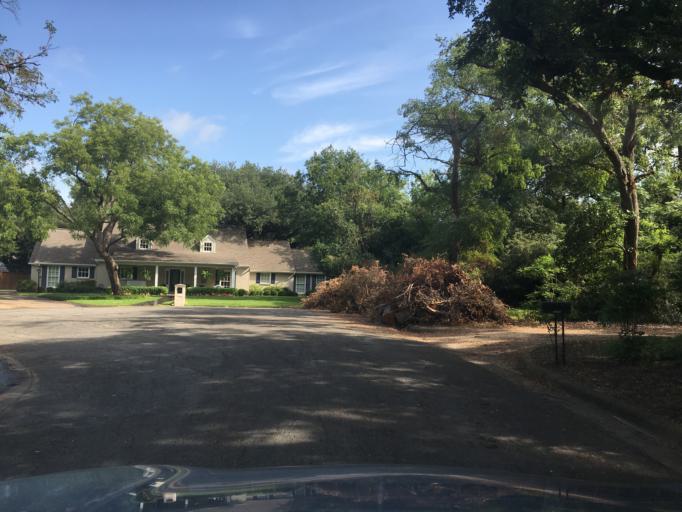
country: US
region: Texas
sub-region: Dallas County
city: Richardson
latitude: 32.9294
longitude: -96.7816
